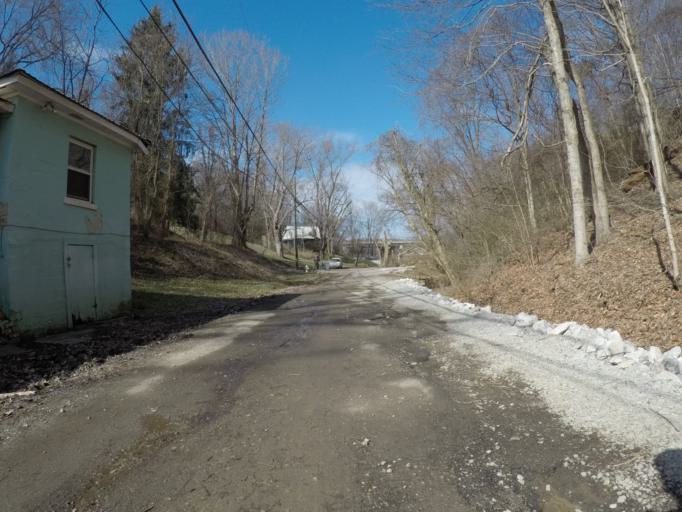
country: US
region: West Virginia
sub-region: Cabell County
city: Huntington
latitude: 38.3992
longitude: -82.4830
